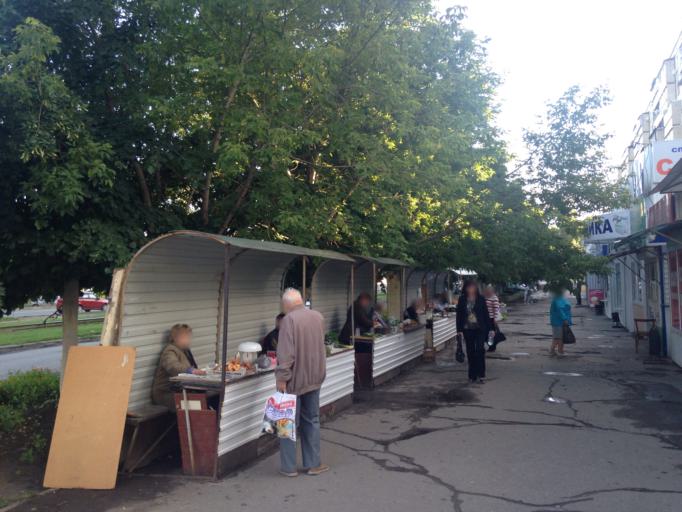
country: RU
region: Ulyanovsk
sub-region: Ulyanovskiy Rayon
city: Ulyanovsk
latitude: 54.2948
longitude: 48.3745
